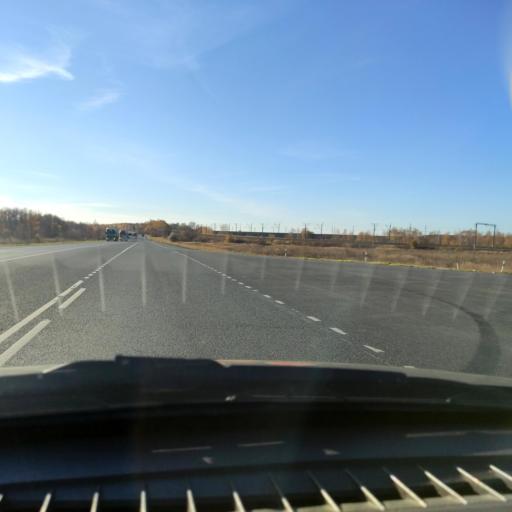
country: RU
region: Samara
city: Mezhdurechensk
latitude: 53.2451
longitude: 48.9942
